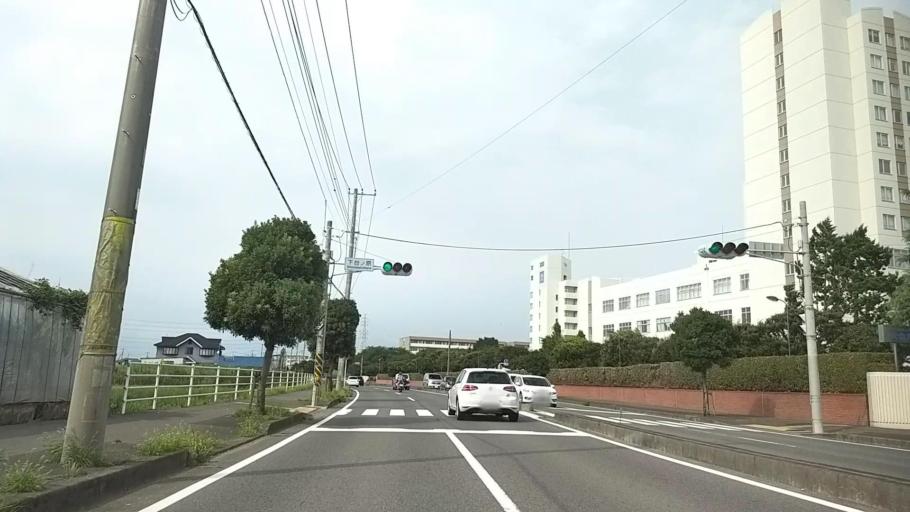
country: JP
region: Kanagawa
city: Atsugi
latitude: 35.4299
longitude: 139.3830
